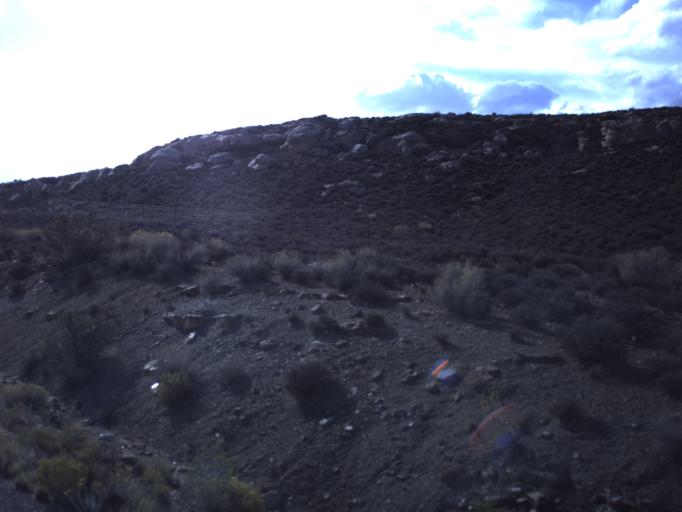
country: US
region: Utah
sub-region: San Juan County
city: Blanding
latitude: 37.3269
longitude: -109.3271
